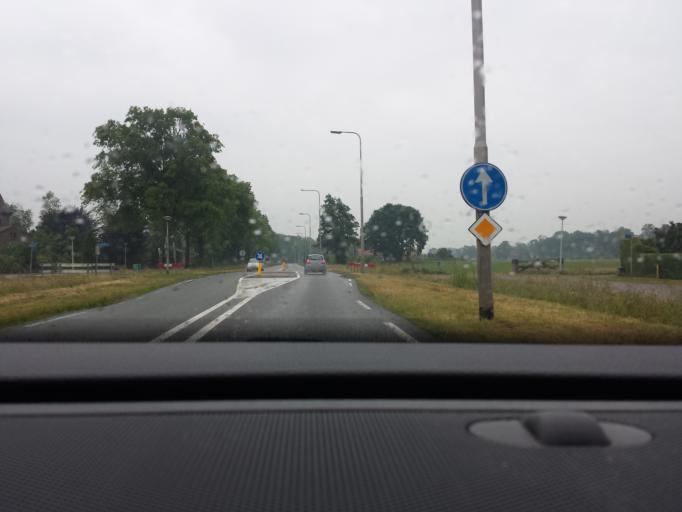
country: NL
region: Overijssel
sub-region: Gemeente Haaksbergen
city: Haaksbergen
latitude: 52.1502
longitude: 6.7358
